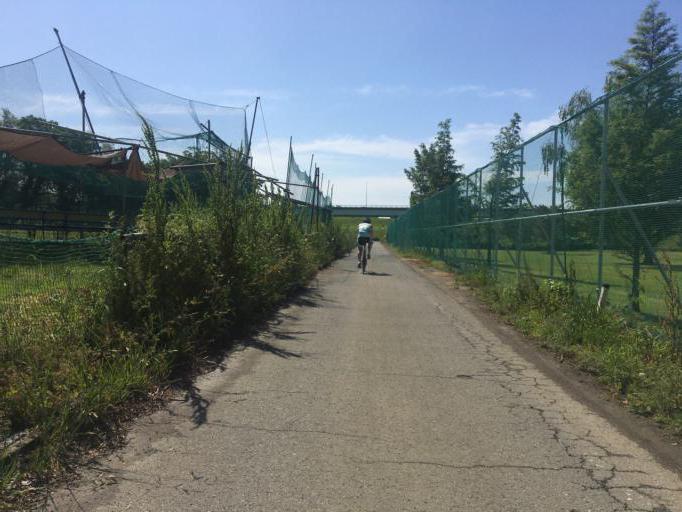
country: JP
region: Saitama
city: Shiki
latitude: 35.8586
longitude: 139.5905
